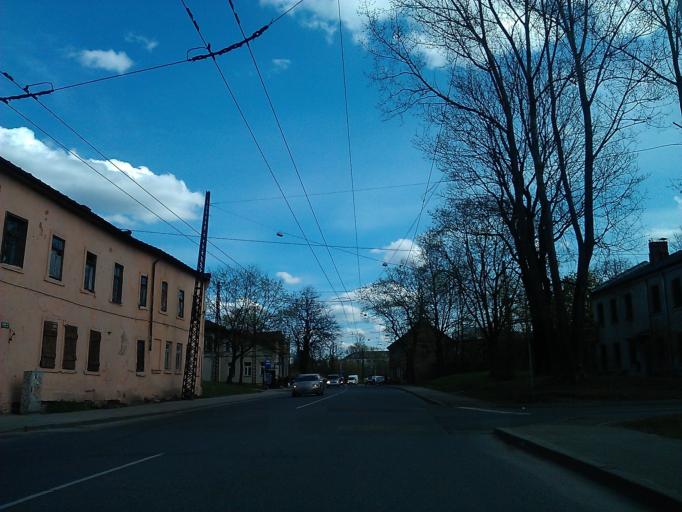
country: LV
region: Riga
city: Riga
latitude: 56.9331
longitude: 24.1656
